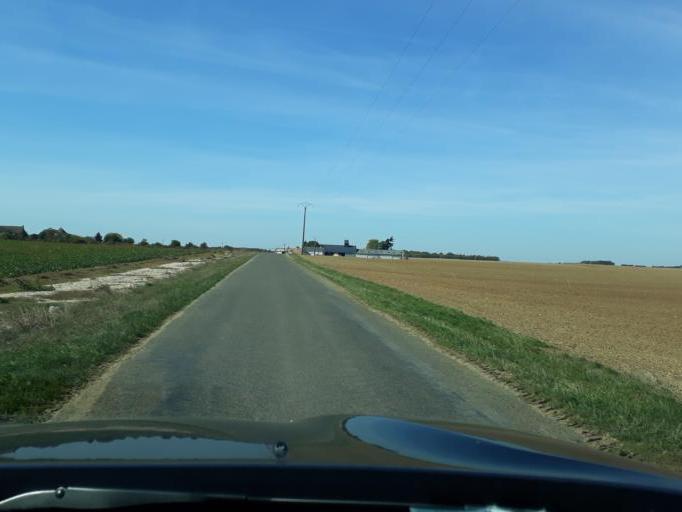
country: FR
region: Centre
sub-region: Departement du Loir-et-Cher
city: Ouzouer-le-Marche
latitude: 47.9426
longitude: 1.5314
